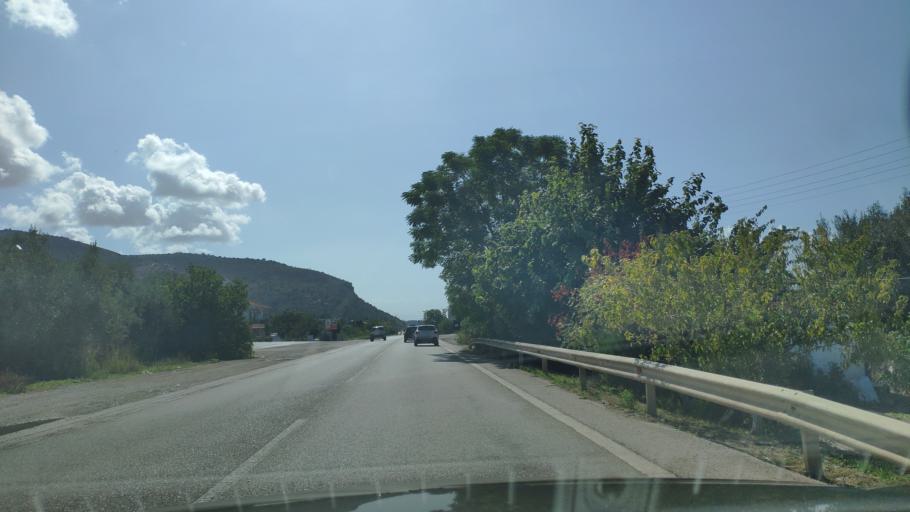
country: GR
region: West Greece
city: Aitoliko
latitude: 38.4701
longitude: 21.3581
